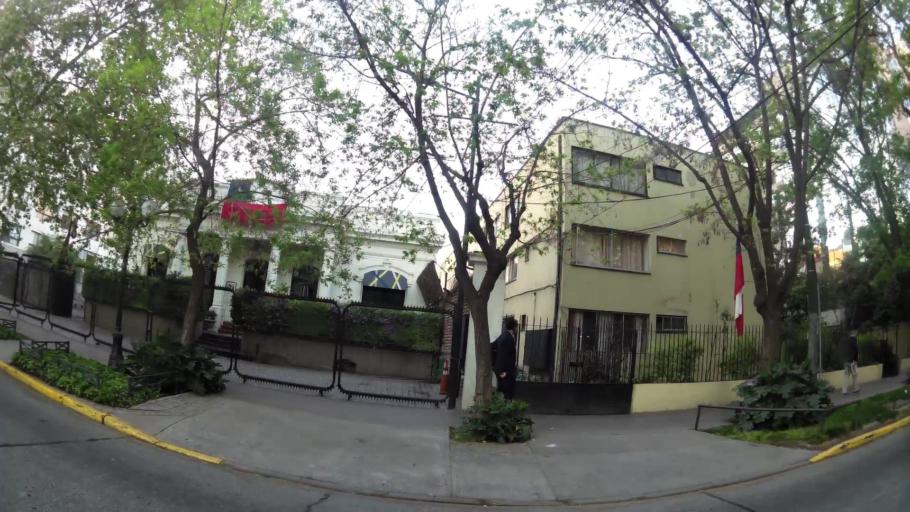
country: CL
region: Santiago Metropolitan
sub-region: Provincia de Santiago
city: Santiago
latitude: -33.4240
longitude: -70.6166
